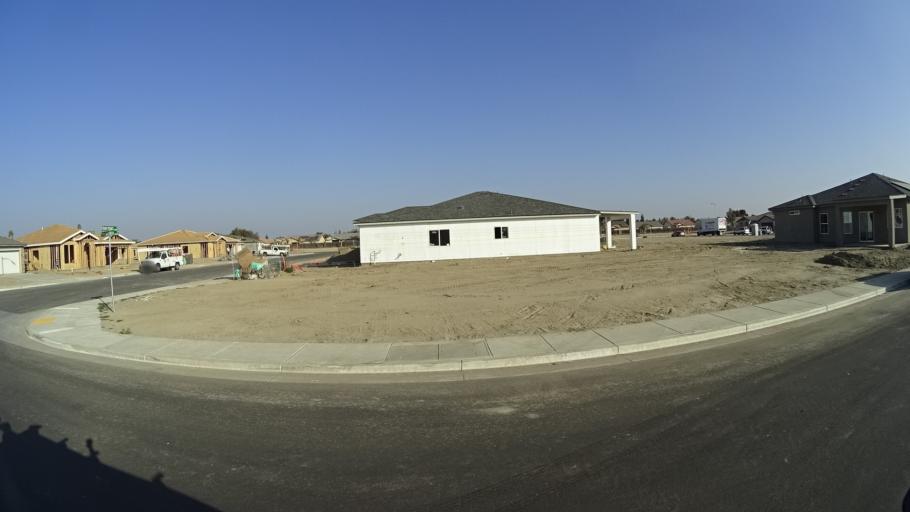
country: US
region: California
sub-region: Kern County
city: Greenfield
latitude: 35.2908
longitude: -119.0180
